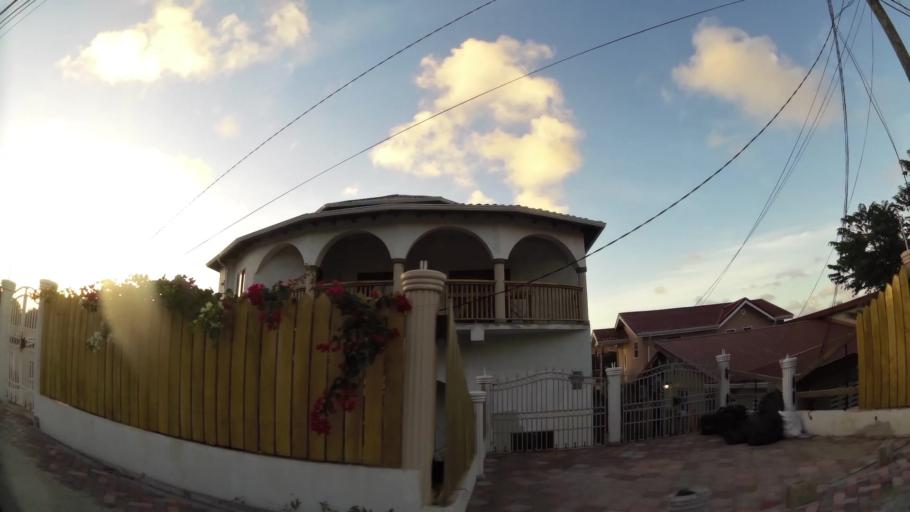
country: LC
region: Gros-Islet
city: Gros Islet
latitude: 14.0666
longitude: -60.9528
